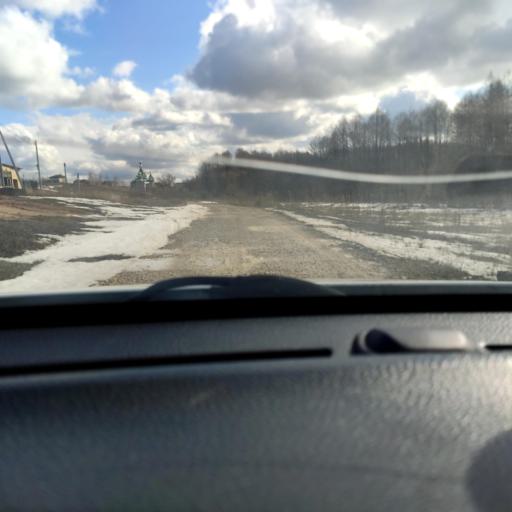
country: RU
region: Voronezj
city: Novaya Usman'
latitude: 51.6855
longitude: 39.3896
